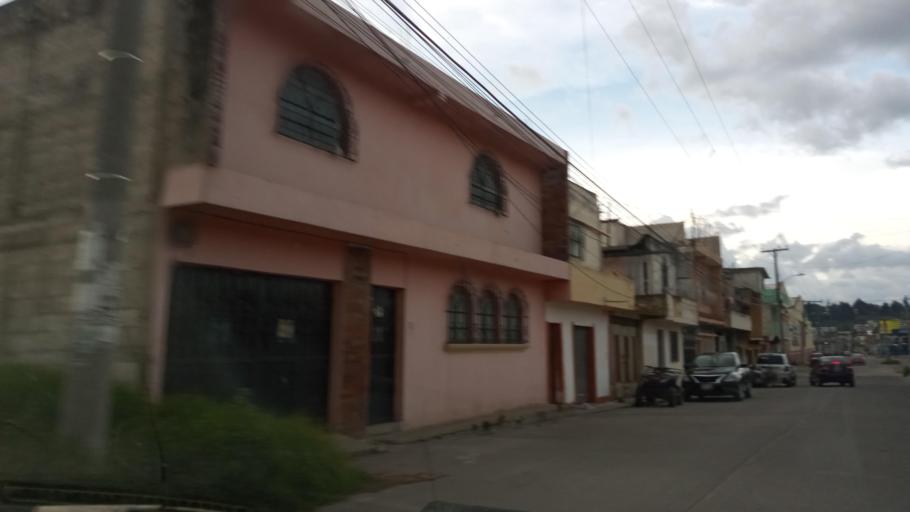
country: GT
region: Quetzaltenango
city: Quetzaltenango
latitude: 14.8398
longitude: -91.5115
